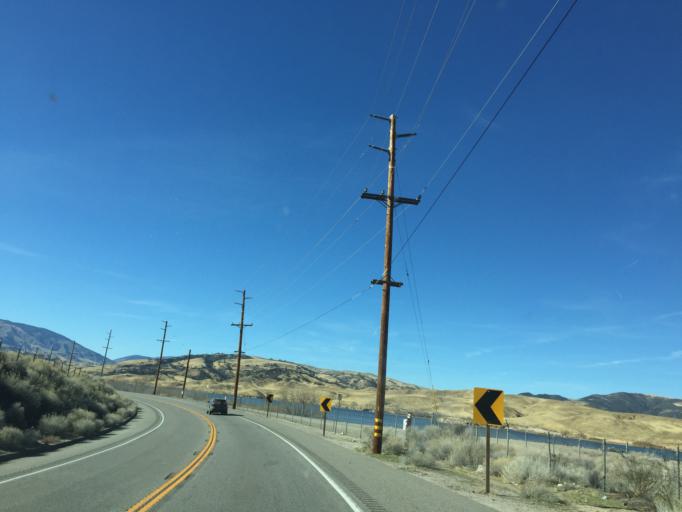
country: US
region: California
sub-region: Kern County
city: Lebec
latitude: 34.7679
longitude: -118.7378
